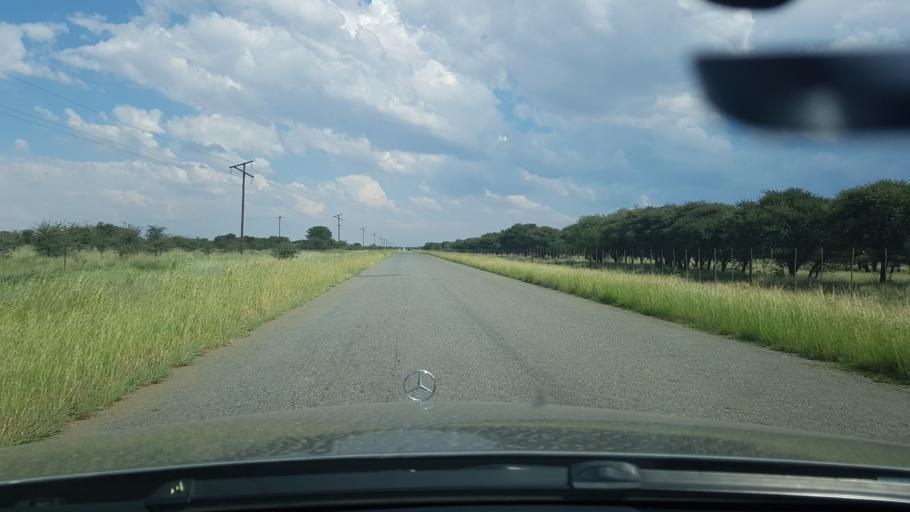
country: ZA
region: North-West
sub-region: Dr Ruth Segomotsi Mompati District Municipality
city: Bloemhof
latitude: -27.7603
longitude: 25.5978
